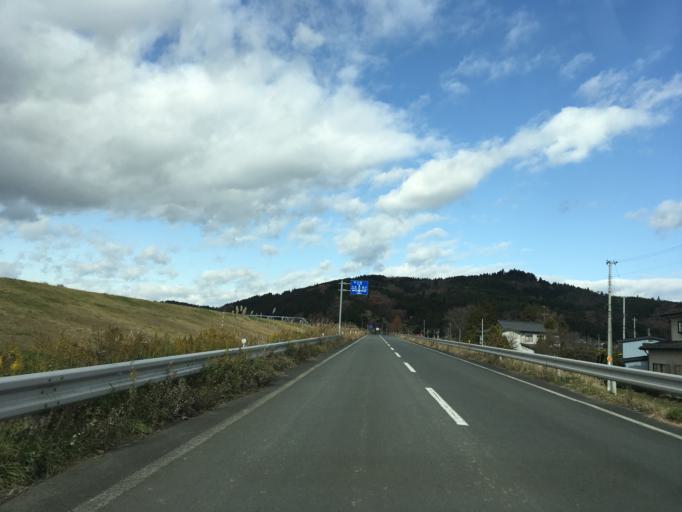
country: JP
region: Iwate
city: Ichinoseki
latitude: 38.8404
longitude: 141.2652
